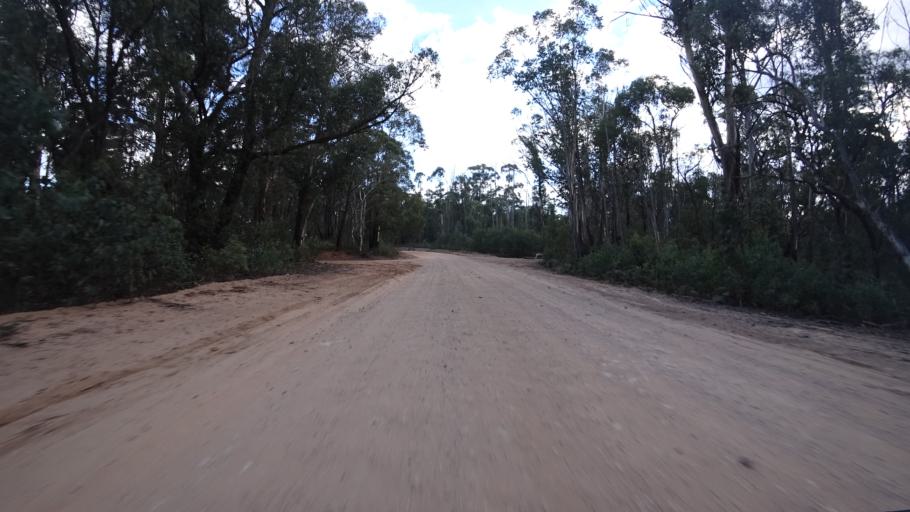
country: AU
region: New South Wales
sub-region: Lithgow
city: Lithgow
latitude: -33.4379
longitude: 150.1825
